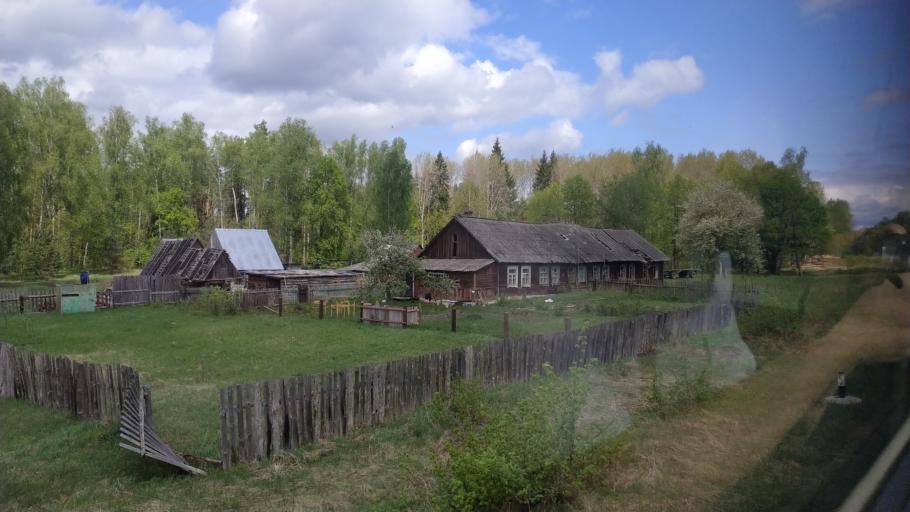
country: RU
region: Kaluga
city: Lyudinovo
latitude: 53.7871
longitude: 34.4098
